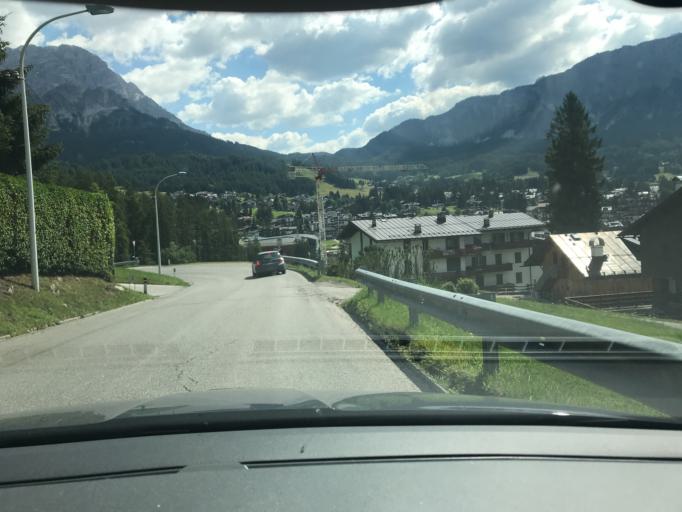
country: IT
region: Veneto
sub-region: Provincia di Belluno
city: Cortina d'Ampezzo
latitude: 46.5434
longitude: 12.1271
